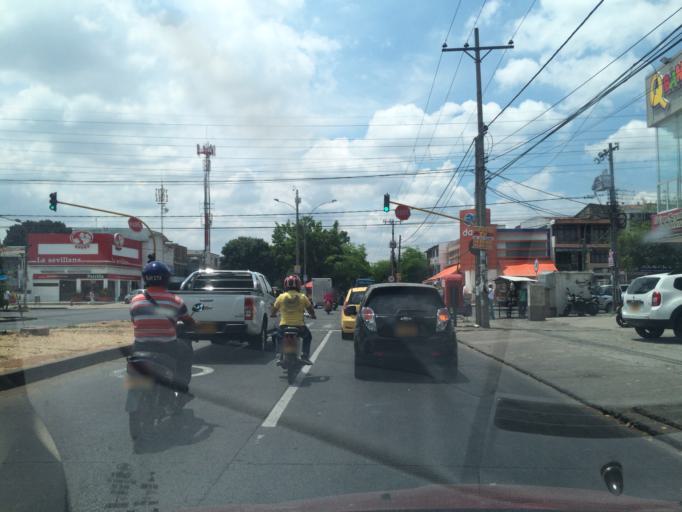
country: CO
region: Valle del Cauca
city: Cali
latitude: 3.4145
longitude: -76.5331
